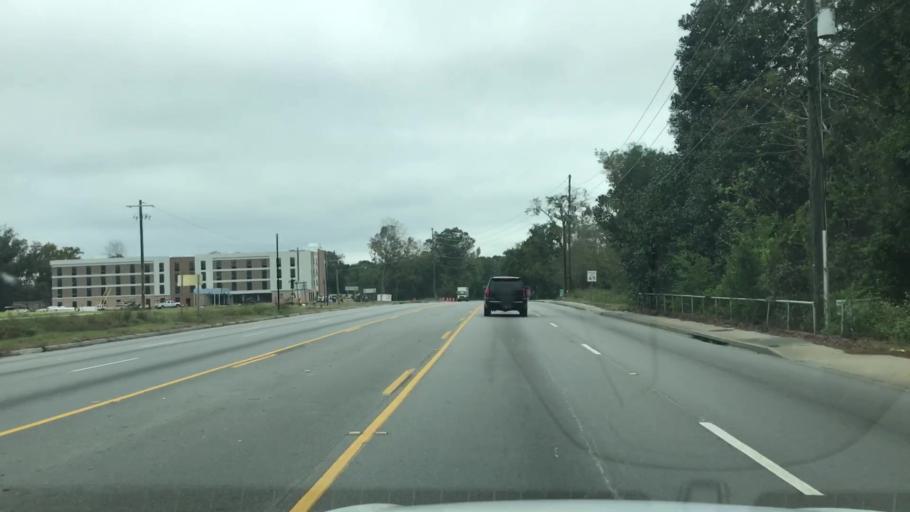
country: US
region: South Carolina
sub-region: Beaufort County
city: Burton
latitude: 32.4420
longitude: -80.7221
